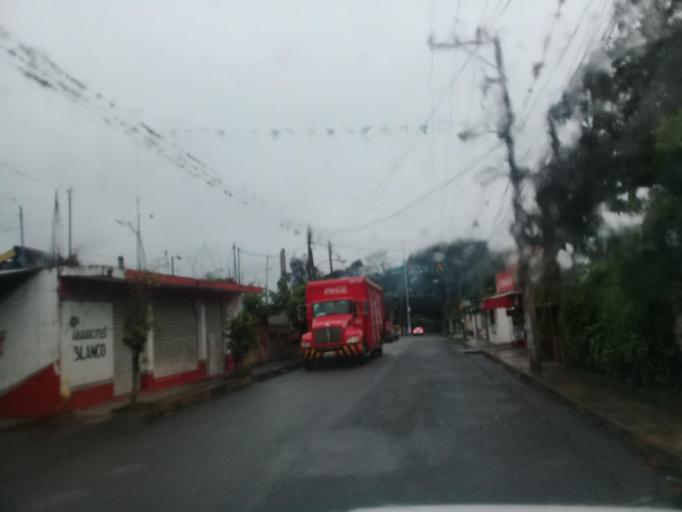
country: MX
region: Veracruz
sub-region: Cordoba
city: San Jose de Tapia
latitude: 18.8489
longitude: -96.9506
